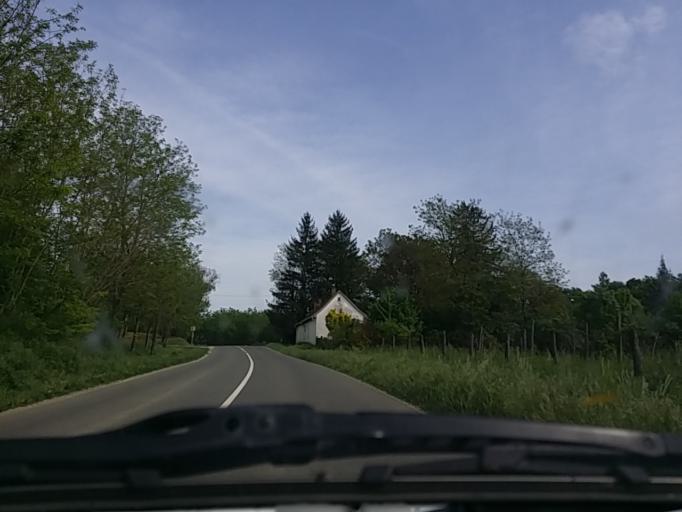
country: HU
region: Baranya
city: Vajszlo
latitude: 45.8404
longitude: 18.0527
